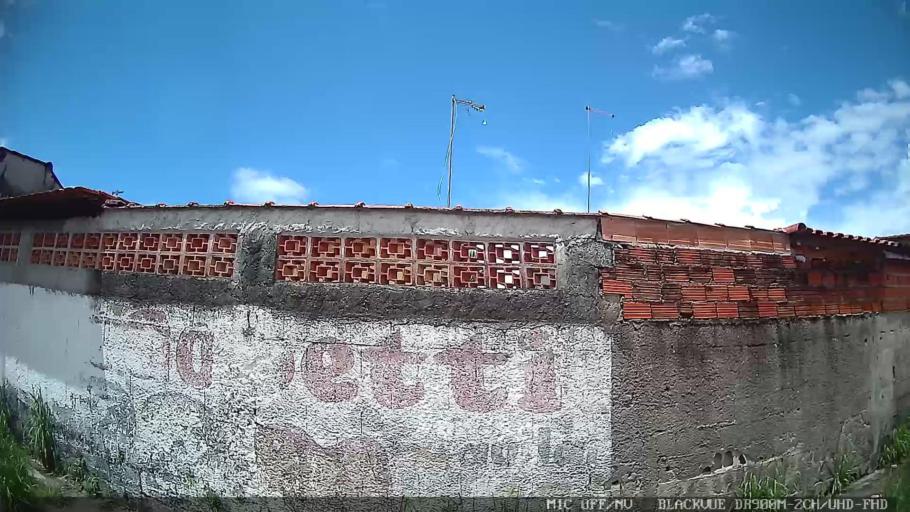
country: BR
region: Sao Paulo
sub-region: Caraguatatuba
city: Caraguatatuba
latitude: -23.6422
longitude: -45.4344
